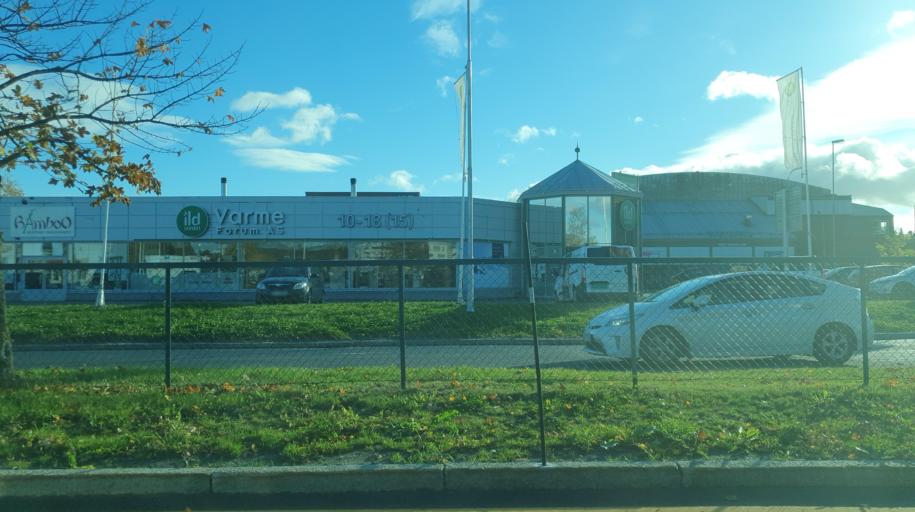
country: NO
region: Sor-Trondelag
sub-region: Trondheim
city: Trondheim
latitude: 63.3601
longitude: 10.3792
